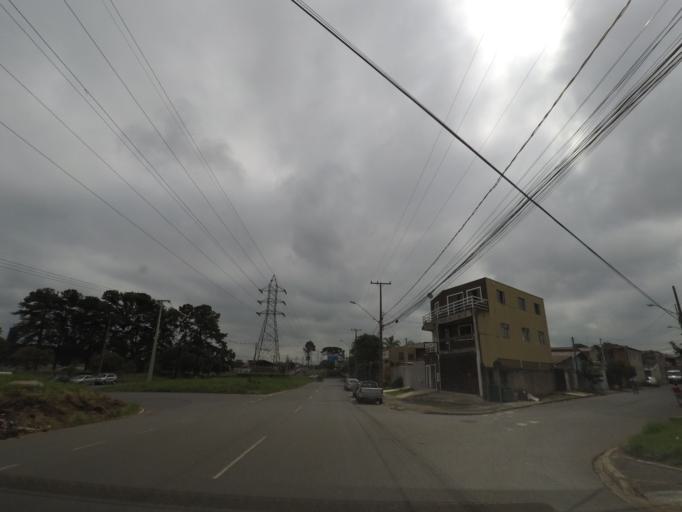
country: BR
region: Parana
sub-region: Curitiba
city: Curitiba
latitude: -25.4921
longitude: -49.3213
